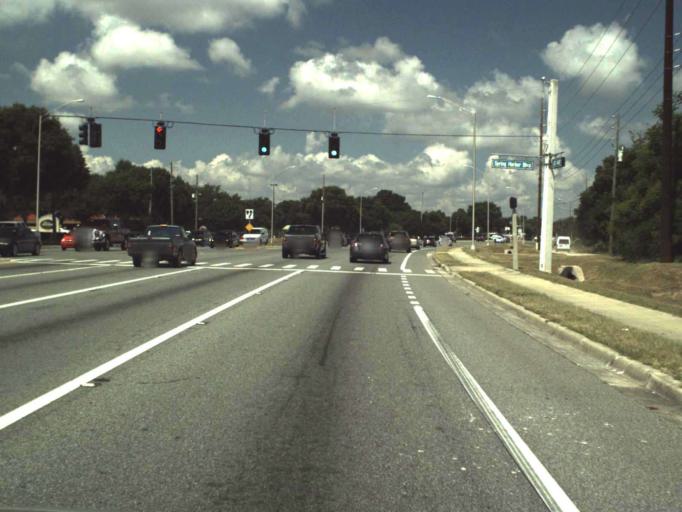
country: US
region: Florida
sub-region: Lake County
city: Mount Dora
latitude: 28.8207
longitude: -81.6704
